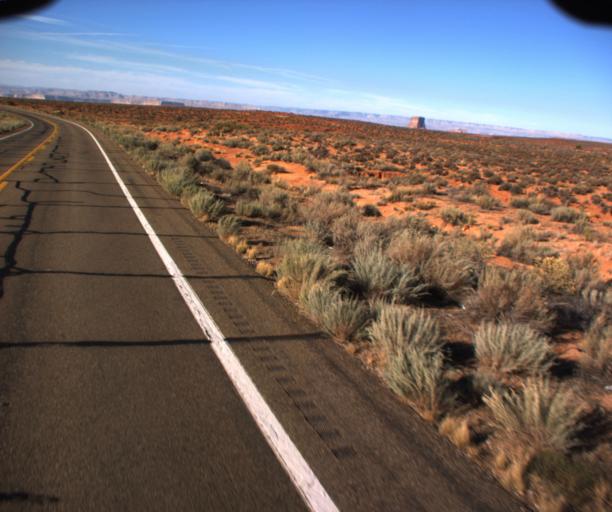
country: US
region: Arizona
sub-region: Coconino County
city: LeChee
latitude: 36.8757
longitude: -111.3432
